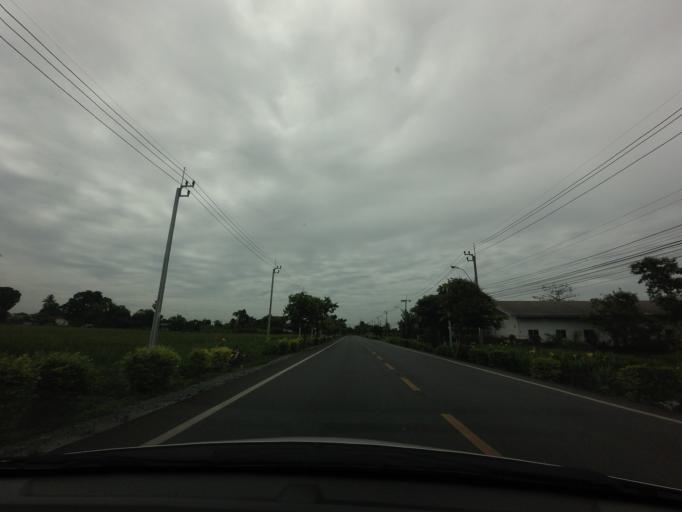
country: TH
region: Pathum Thani
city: Lam Luk Ka
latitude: 13.8990
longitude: 100.7944
